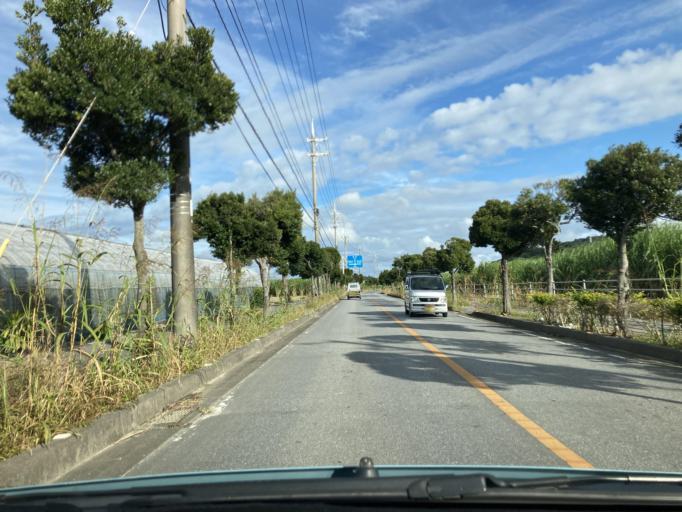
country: JP
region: Okinawa
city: Itoman
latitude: 26.1353
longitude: 127.7058
